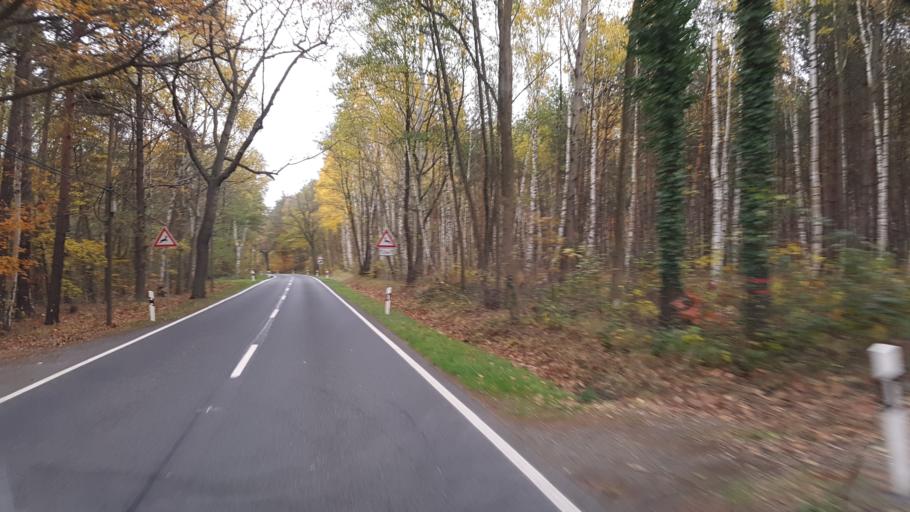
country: DE
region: Brandenburg
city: Crinitz
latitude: 51.7448
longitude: 13.7824
